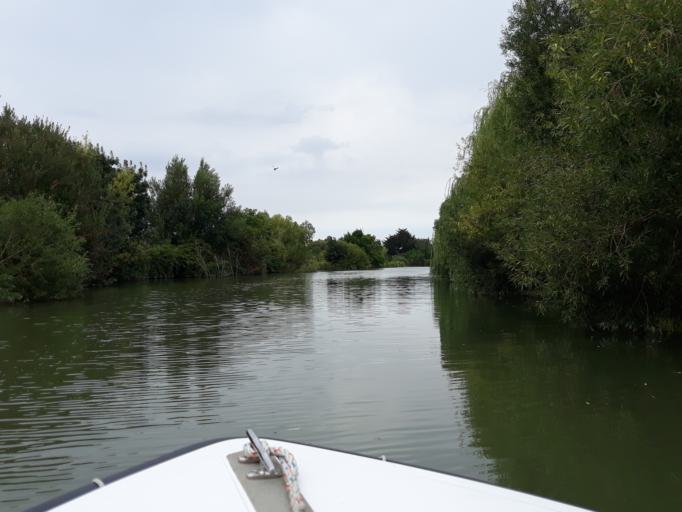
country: FR
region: Poitou-Charentes
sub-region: Departement de la Charente-Maritime
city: Marans
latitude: 46.3177
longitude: -0.9469
